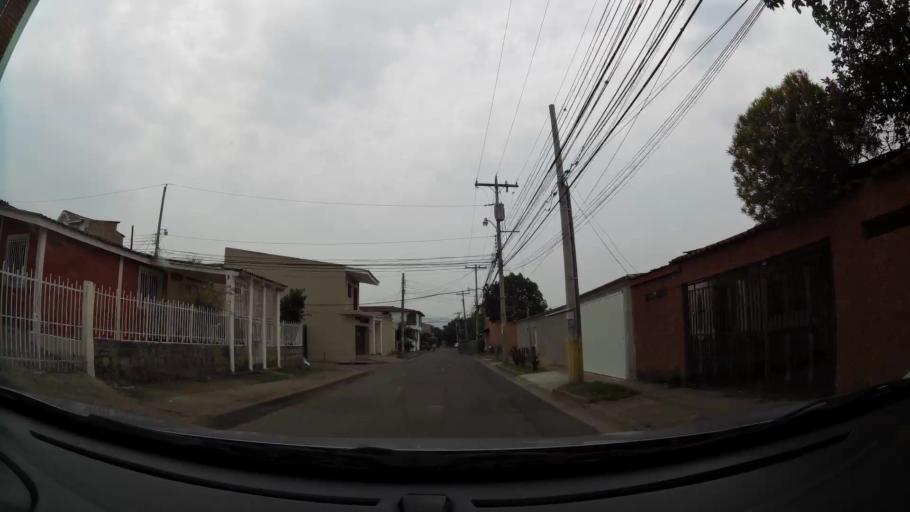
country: HN
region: Francisco Morazan
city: Tegucigalpa
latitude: 14.0718
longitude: -87.1940
